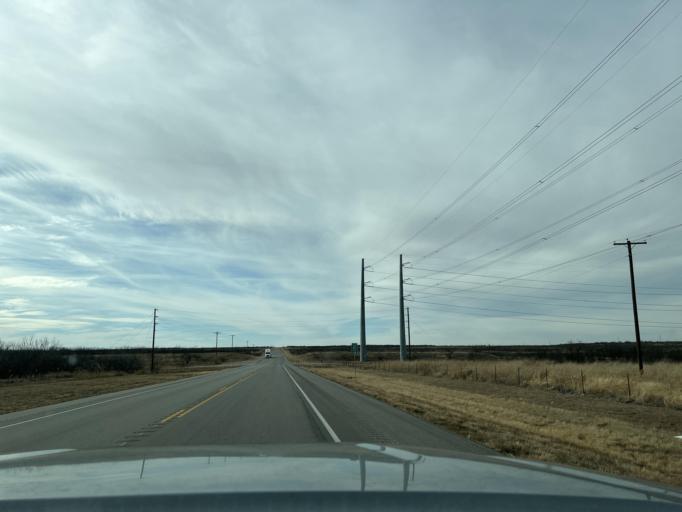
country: US
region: Texas
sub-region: Jones County
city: Anson
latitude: 32.7504
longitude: -99.6510
